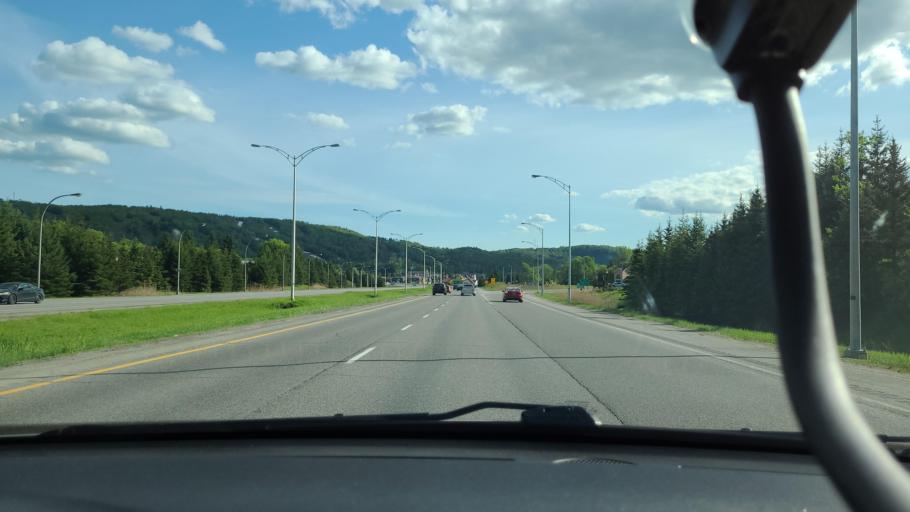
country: CA
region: Quebec
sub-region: Laurentides
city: Saint-Sauveur
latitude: 45.8983
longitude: -74.1448
